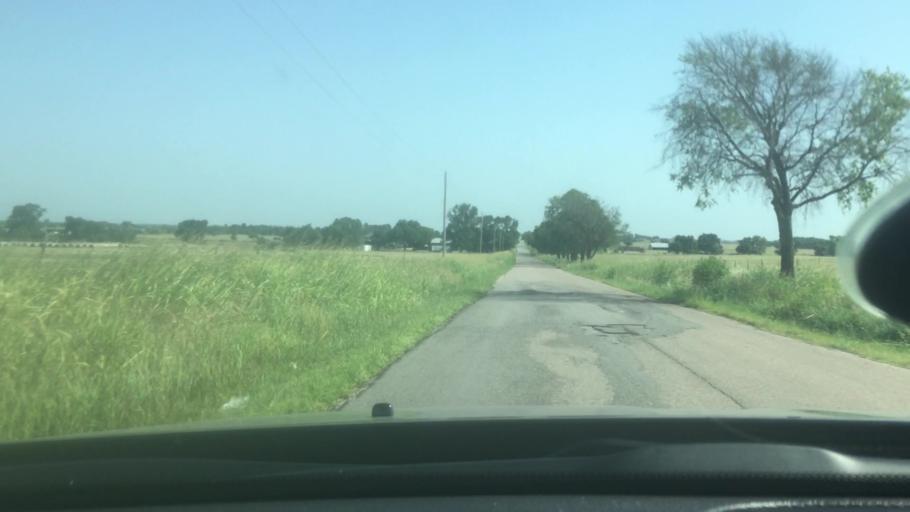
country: US
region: Oklahoma
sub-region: Bryan County
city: Calera
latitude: 33.9779
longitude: -96.4656
